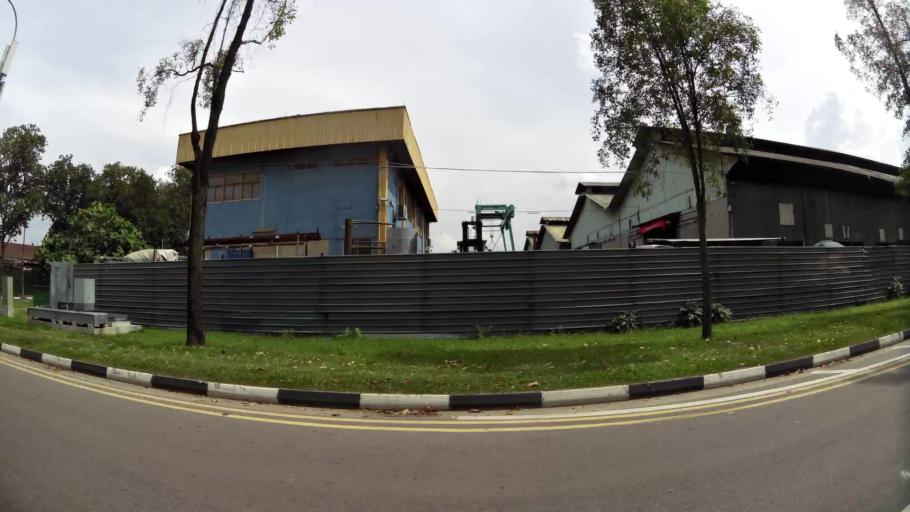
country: MY
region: Johor
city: Johor Bahru
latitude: 1.4242
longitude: 103.7451
